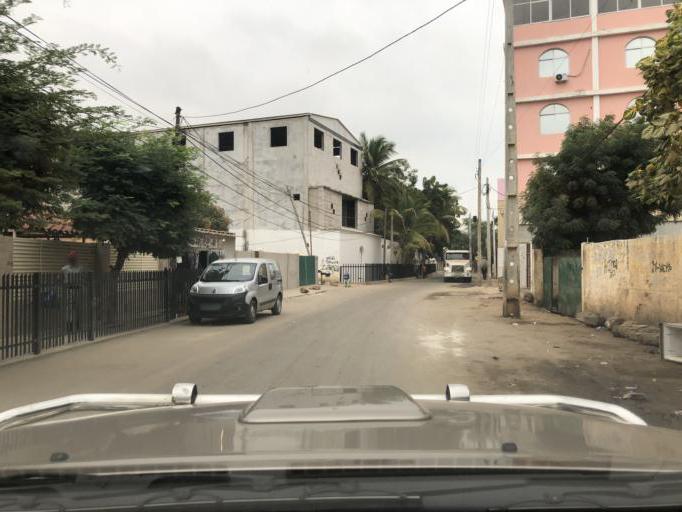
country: AO
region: Luanda
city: Luanda
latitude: -8.9046
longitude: 13.1632
